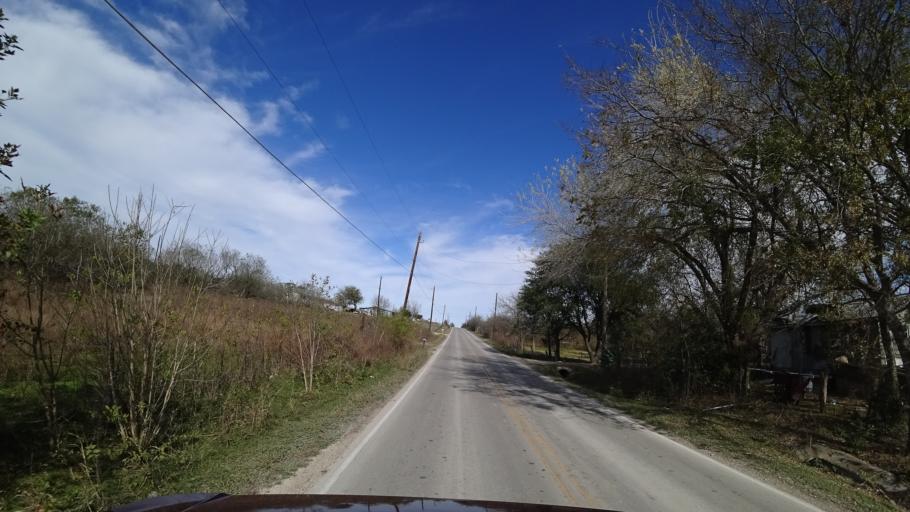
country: US
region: Texas
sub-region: Travis County
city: Onion Creek
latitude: 30.1291
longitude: -97.7377
